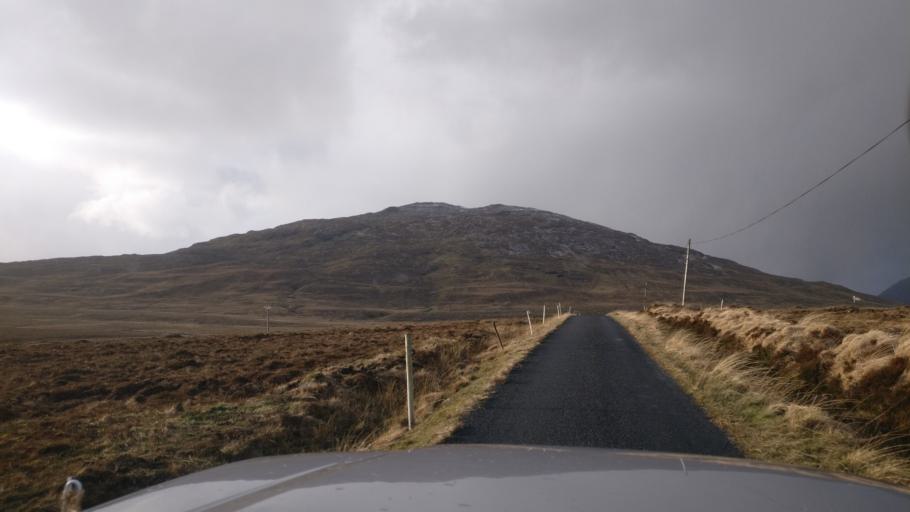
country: IE
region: Connaught
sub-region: County Galway
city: Clifden
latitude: 53.4728
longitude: -9.6913
